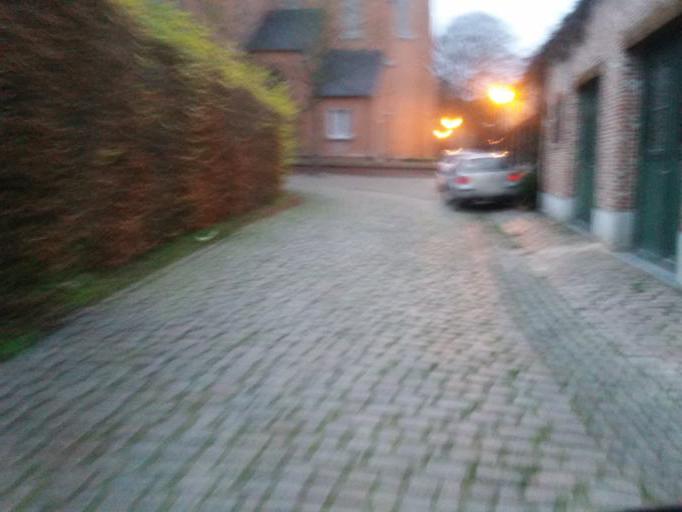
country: BE
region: Flanders
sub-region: Provincie Antwerpen
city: Lier
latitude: 51.1623
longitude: 4.6077
